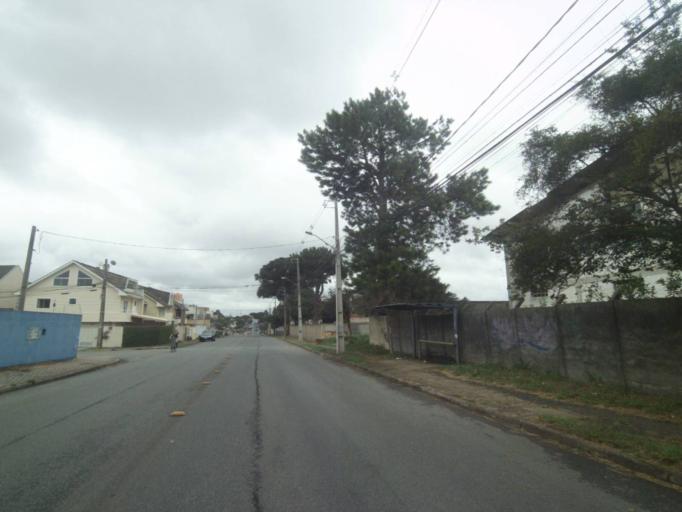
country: BR
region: Parana
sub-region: Curitiba
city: Curitiba
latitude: -25.4911
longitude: -49.2996
